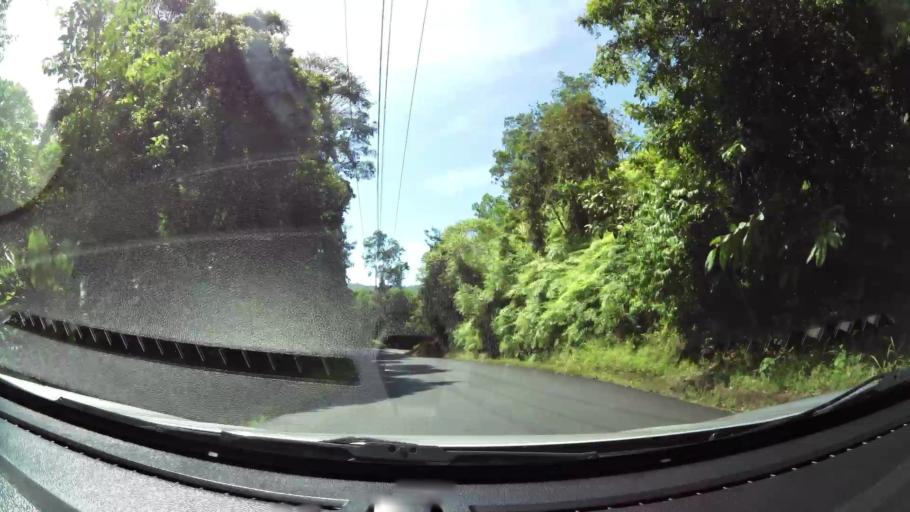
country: CR
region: San Jose
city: San Isidro
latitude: 9.2799
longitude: -83.8265
